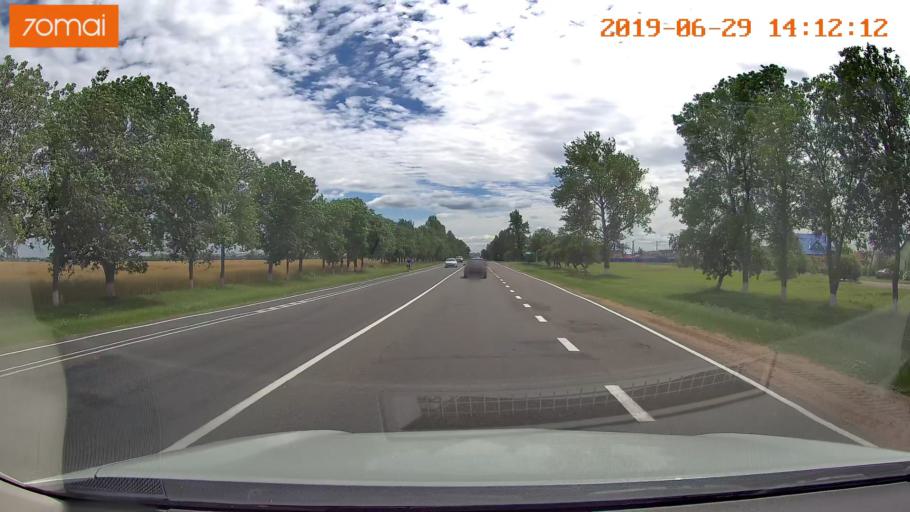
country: BY
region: Minsk
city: Salihorsk
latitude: 52.8124
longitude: 27.5064
